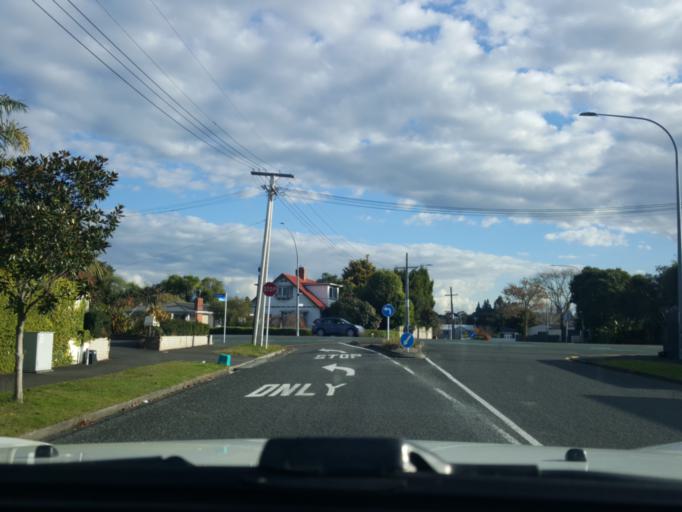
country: NZ
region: Waikato
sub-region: Hamilton City
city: Hamilton
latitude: -37.7718
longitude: 175.2642
